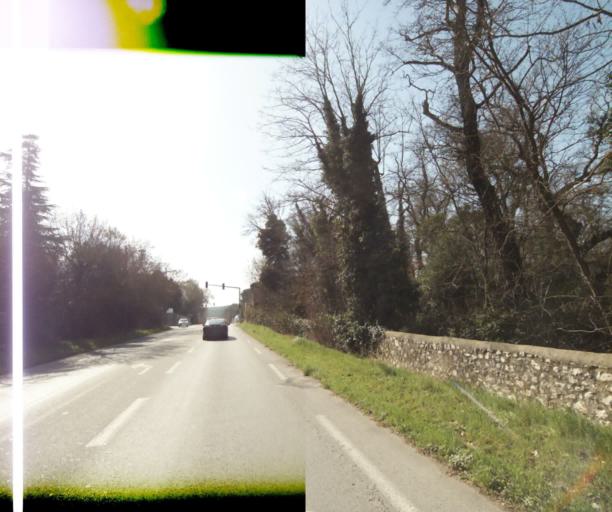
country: FR
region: Provence-Alpes-Cote d'Azur
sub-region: Departement des Bouches-du-Rhone
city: Bouc-Bel-Air
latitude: 43.4536
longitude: 5.4011
